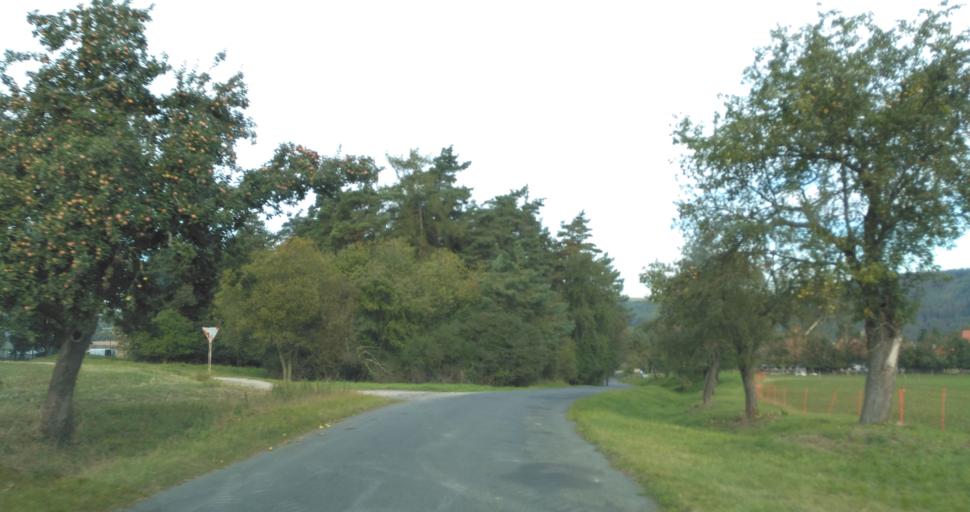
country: CZ
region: Plzensky
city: Zbiroh
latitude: 49.9603
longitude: 13.7697
